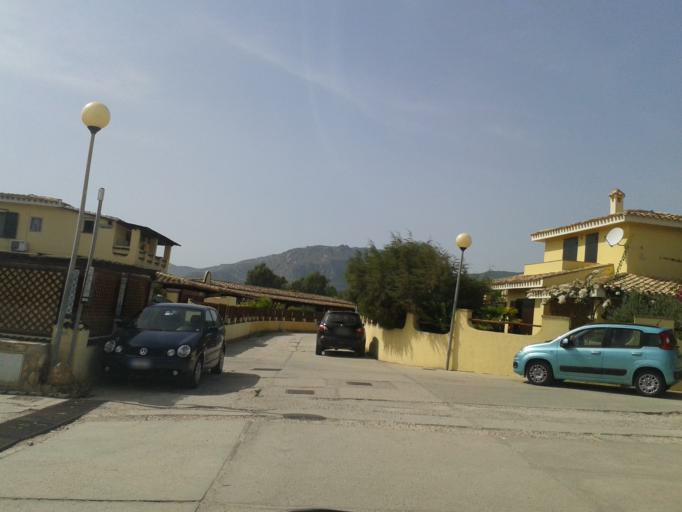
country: IT
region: Sardinia
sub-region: Provincia di Cagliari
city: Villasimius
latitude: 39.1287
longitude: 9.5099
